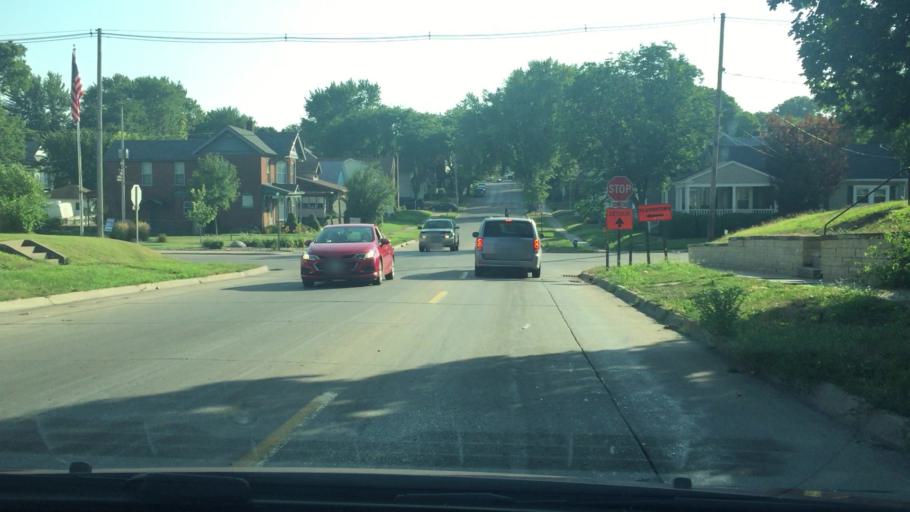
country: US
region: Iowa
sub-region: Muscatine County
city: Muscatine
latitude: 41.4275
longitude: -91.0479
